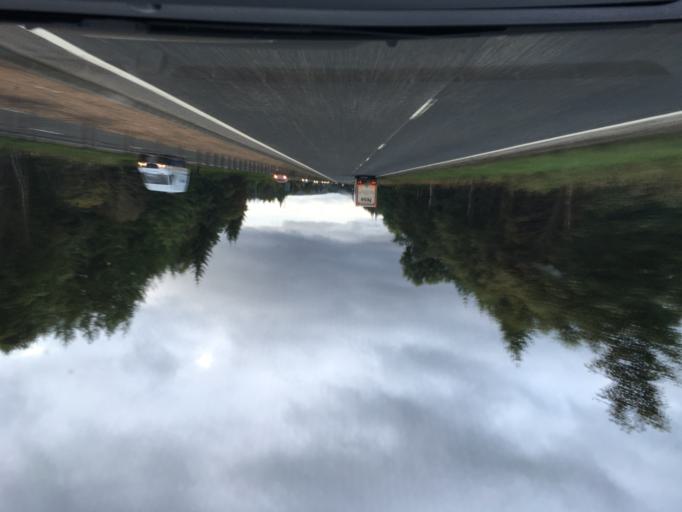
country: GB
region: Scotland
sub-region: Highland
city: Inverness
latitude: 57.4452
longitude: -4.1503
